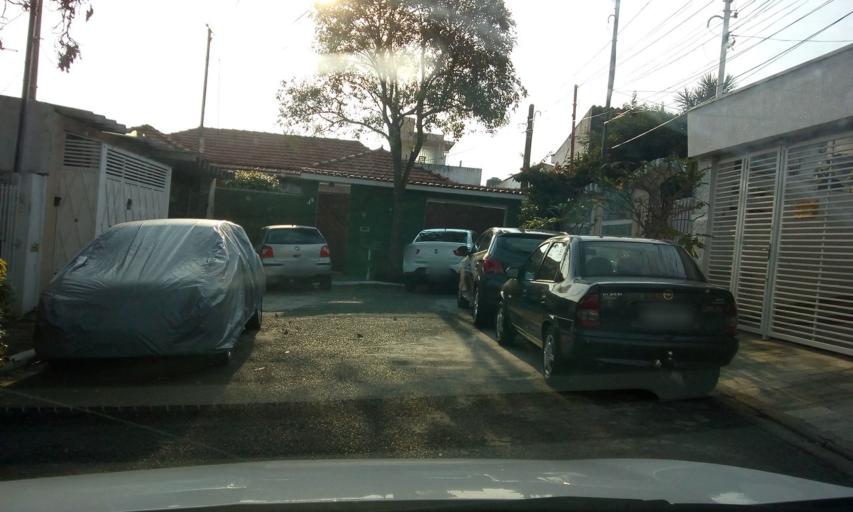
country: BR
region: Sao Paulo
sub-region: Diadema
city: Diadema
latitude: -23.6194
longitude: -46.6549
